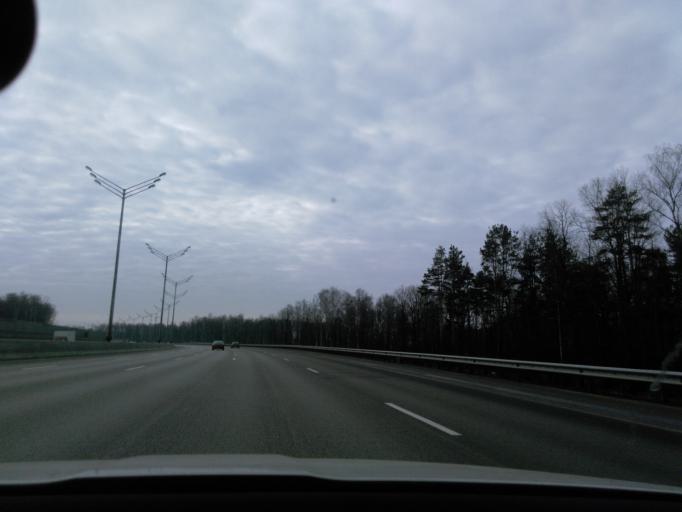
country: RU
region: Moscow
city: Khimki
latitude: 55.9210
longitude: 37.4556
